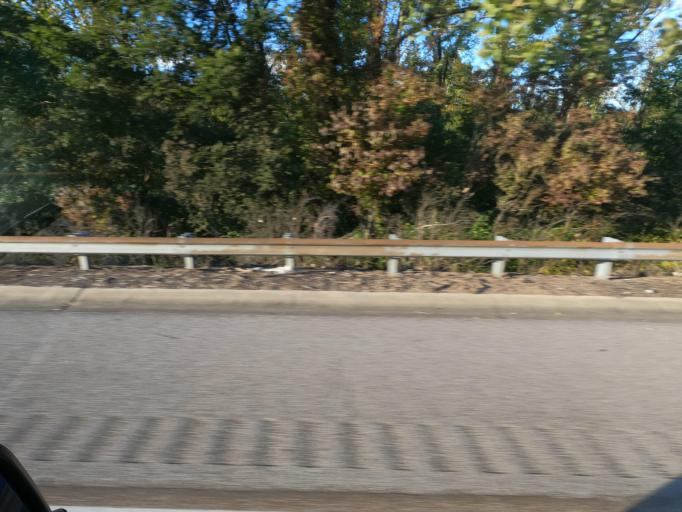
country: US
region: Tennessee
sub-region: Shelby County
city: Millington
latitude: 35.3306
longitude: -89.9073
